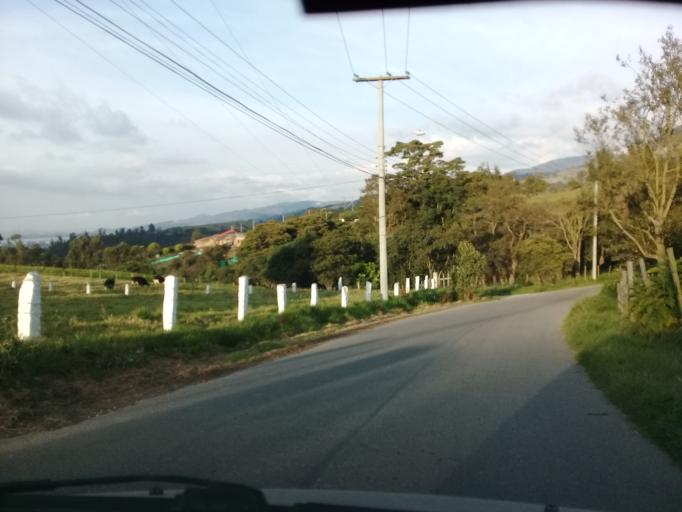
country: CO
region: Cundinamarca
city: Sibate
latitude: 4.4608
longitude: -74.2670
